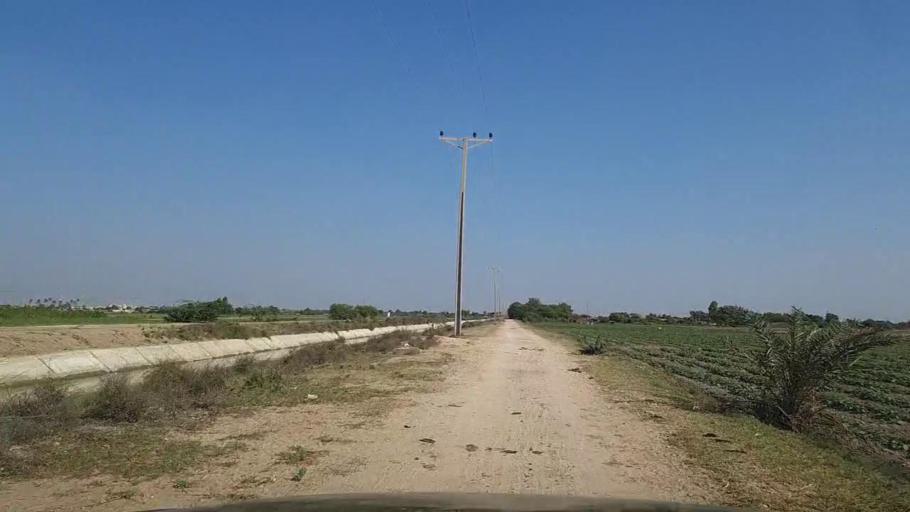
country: PK
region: Sindh
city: Mirpur Sakro
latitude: 24.5968
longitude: 67.8057
